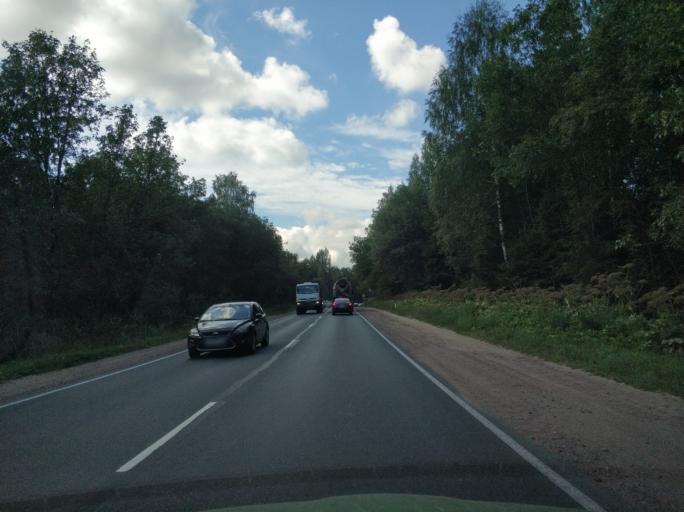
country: RU
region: Leningrad
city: Vsevolozhsk
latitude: 60.0399
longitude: 30.6713
